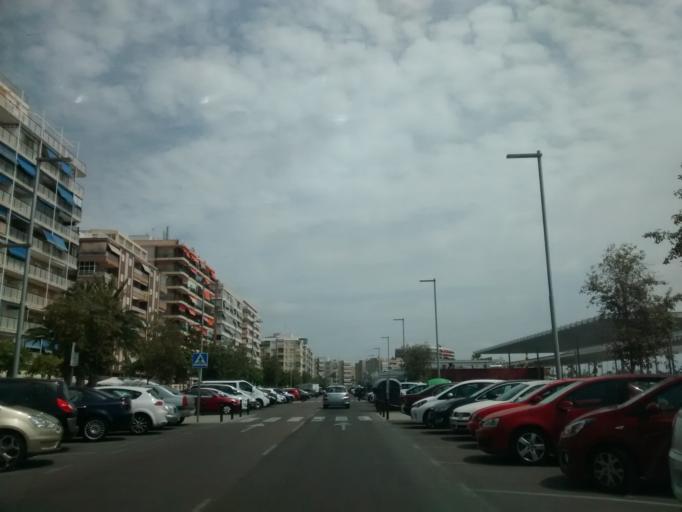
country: ES
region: Valencia
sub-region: Provincia de Alicante
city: Santa Pola
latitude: 38.1912
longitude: -0.5646
